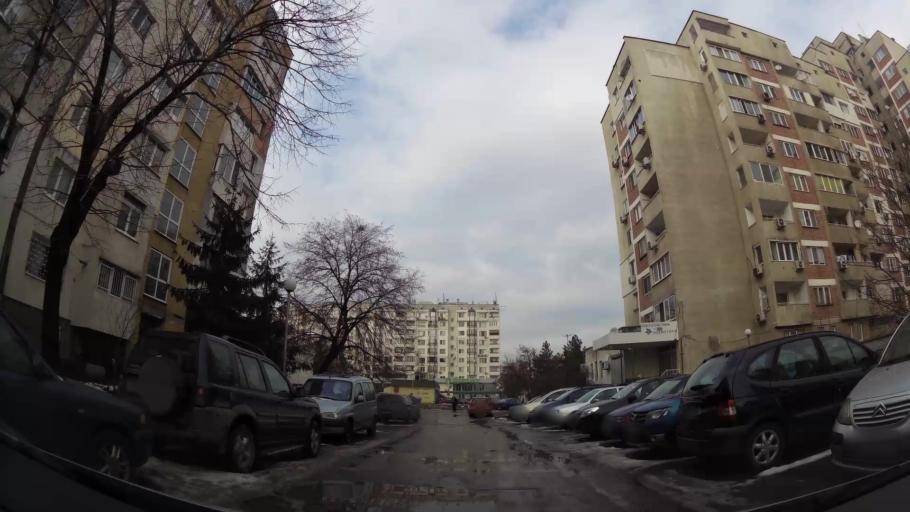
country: BG
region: Sofiya
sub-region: Obshtina Bozhurishte
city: Bozhurishte
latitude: 42.7148
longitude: 23.2514
